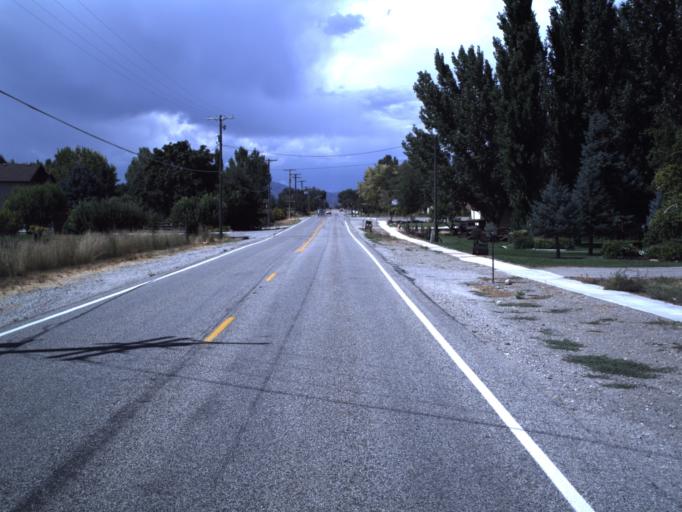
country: US
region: Utah
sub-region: Box Elder County
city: Honeyville
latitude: 41.6107
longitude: -112.0623
